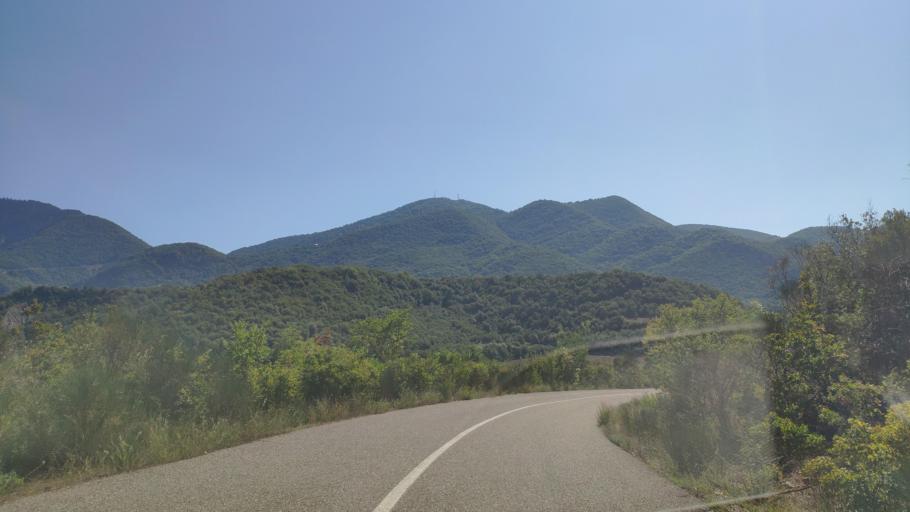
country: GR
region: Central Greece
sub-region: Nomos Evrytanias
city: Kerasochori
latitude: 38.9986
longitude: 21.5543
